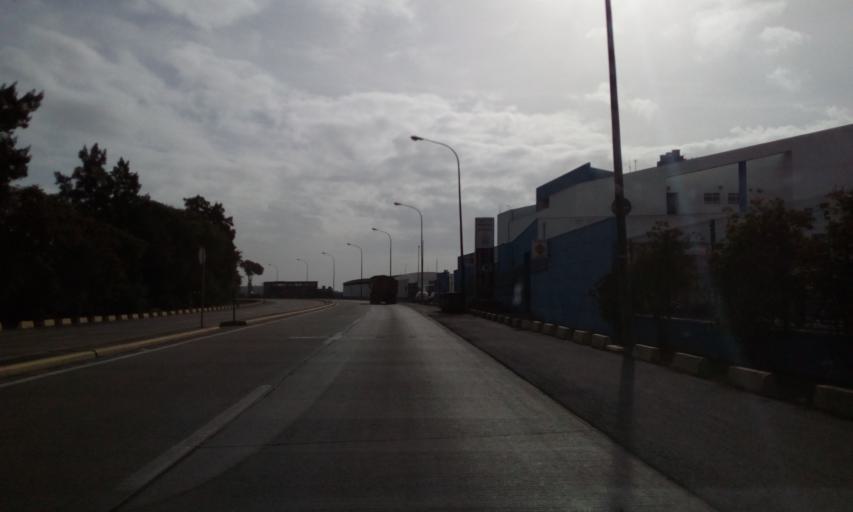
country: ES
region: Andalusia
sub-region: Provincia de Huelva
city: Punta Umbria
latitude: 37.2167
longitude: -6.9466
